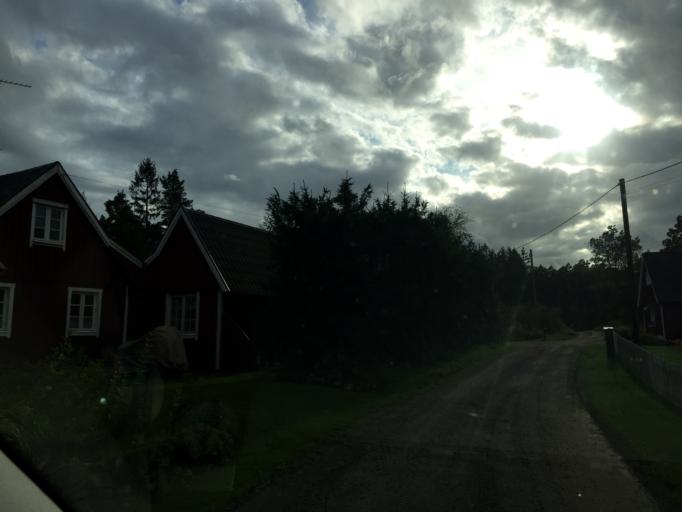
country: SE
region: Skane
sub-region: Perstorps Kommun
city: Perstorp
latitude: 56.2127
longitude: 13.3525
